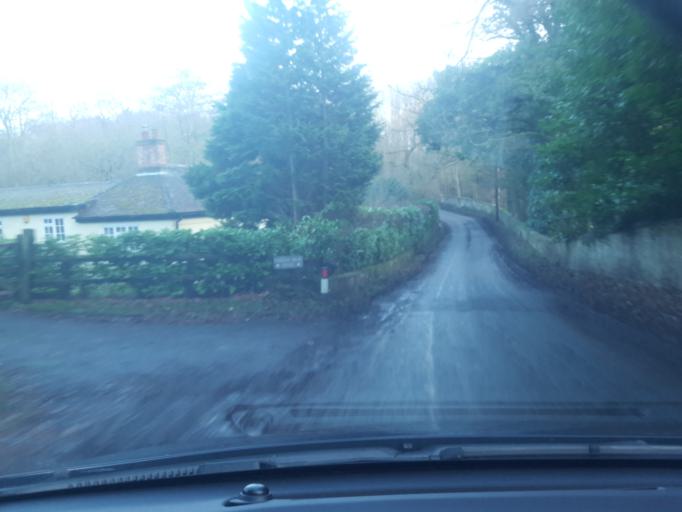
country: GB
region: England
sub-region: Shropshire
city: Tong
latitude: 52.6576
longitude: -2.3211
